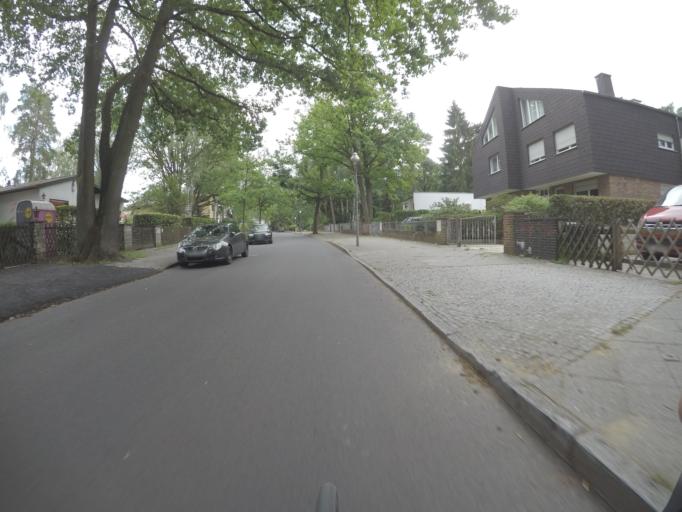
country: DE
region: Berlin
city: Frohnau
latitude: 52.6280
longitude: 13.2666
